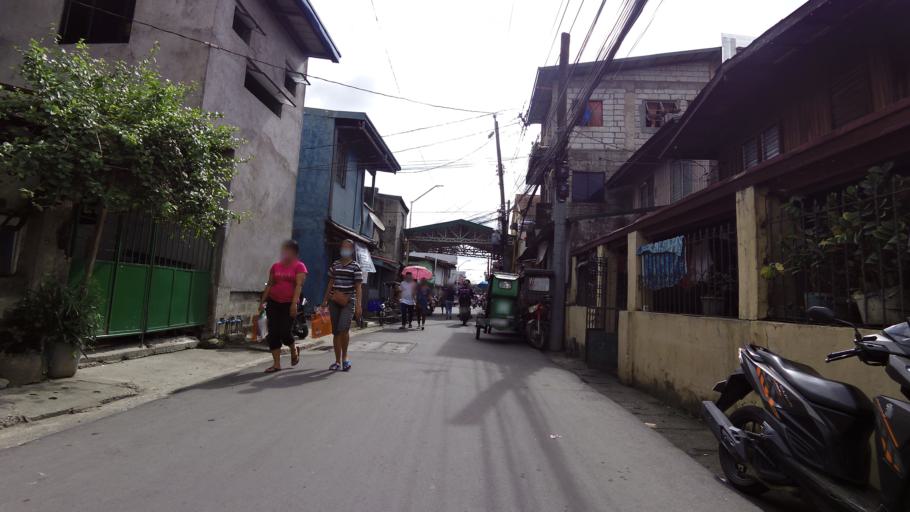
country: PH
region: Calabarzon
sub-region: Province of Rizal
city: Cainta
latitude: 14.5726
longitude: 121.1217
